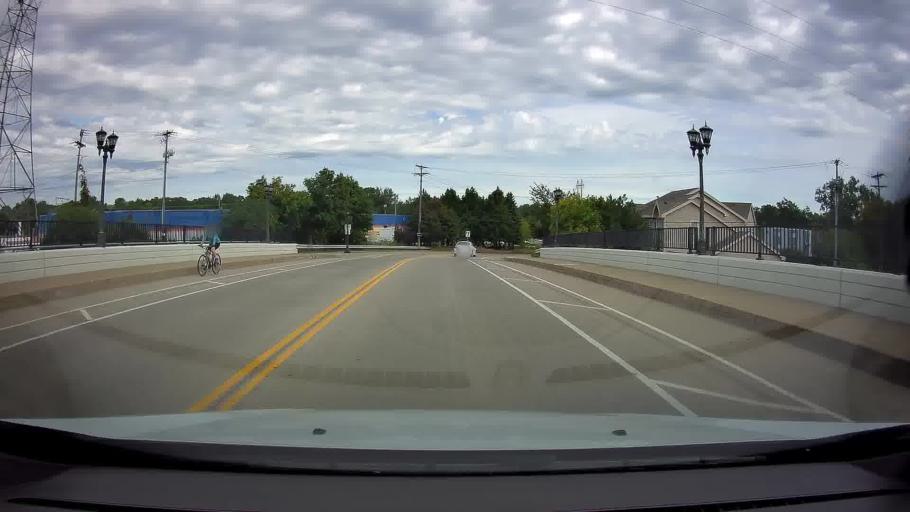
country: US
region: Minnesota
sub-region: Ramsey County
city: Lauderdale
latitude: 44.9731
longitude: -93.1956
